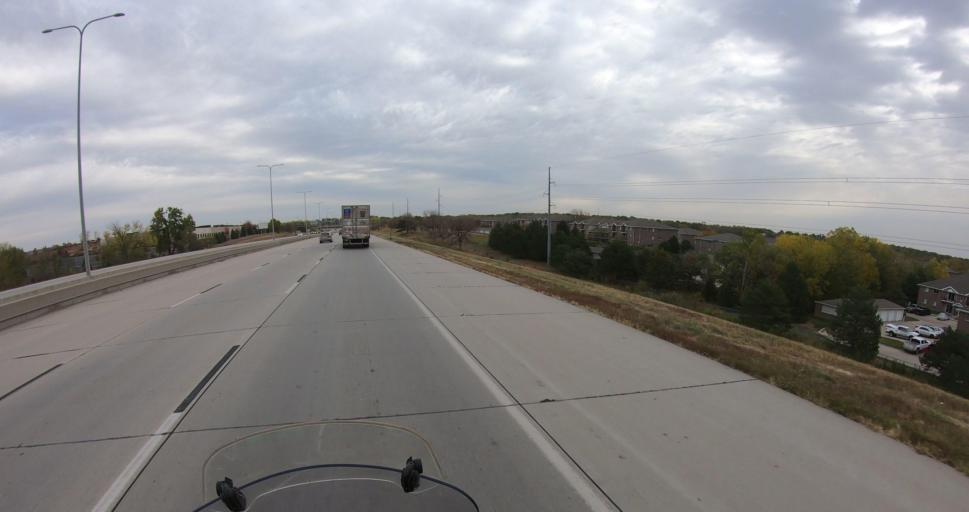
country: US
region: Nebraska
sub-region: Lancaster County
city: Lincoln
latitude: 40.8538
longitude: -96.7261
